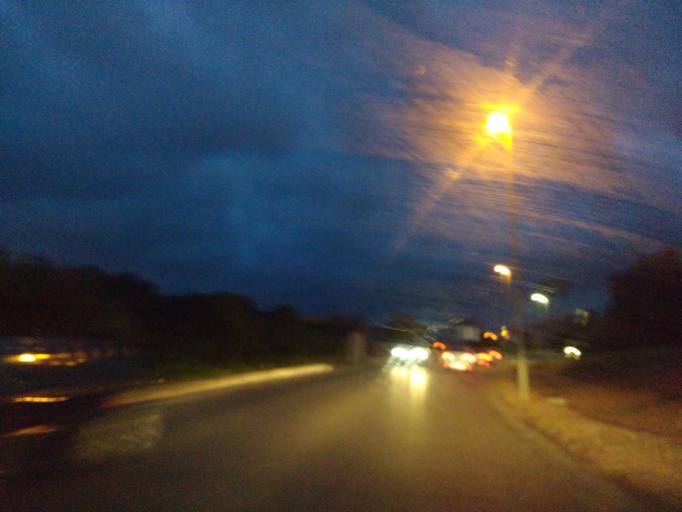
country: IT
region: Latium
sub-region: Citta metropolitana di Roma Capitale
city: Anzio
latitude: 41.4552
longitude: 12.6217
